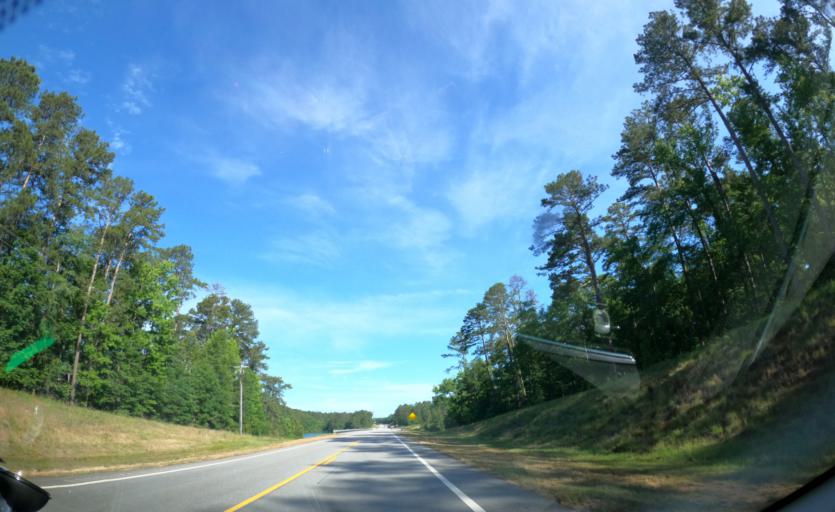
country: US
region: Georgia
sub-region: Columbia County
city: Appling
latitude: 33.6400
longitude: -82.3056
